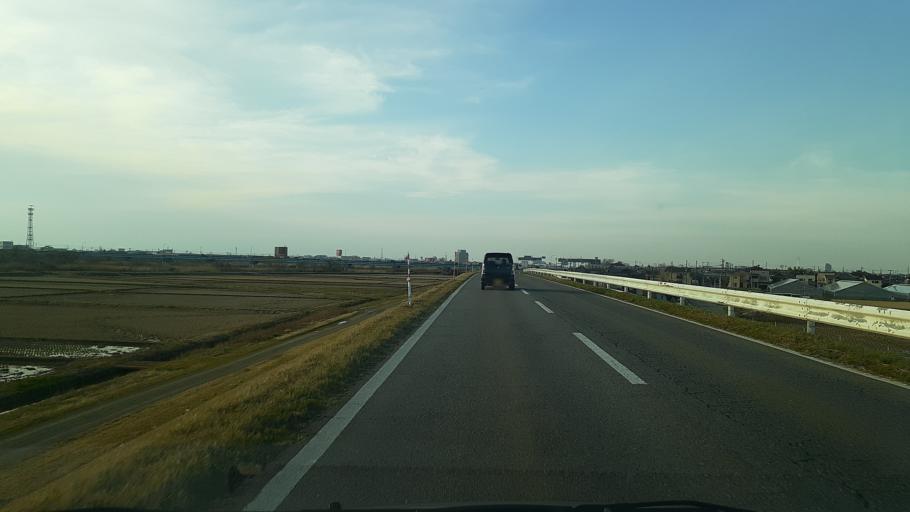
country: JP
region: Niigata
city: Niigata-shi
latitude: 37.8507
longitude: 139.0268
